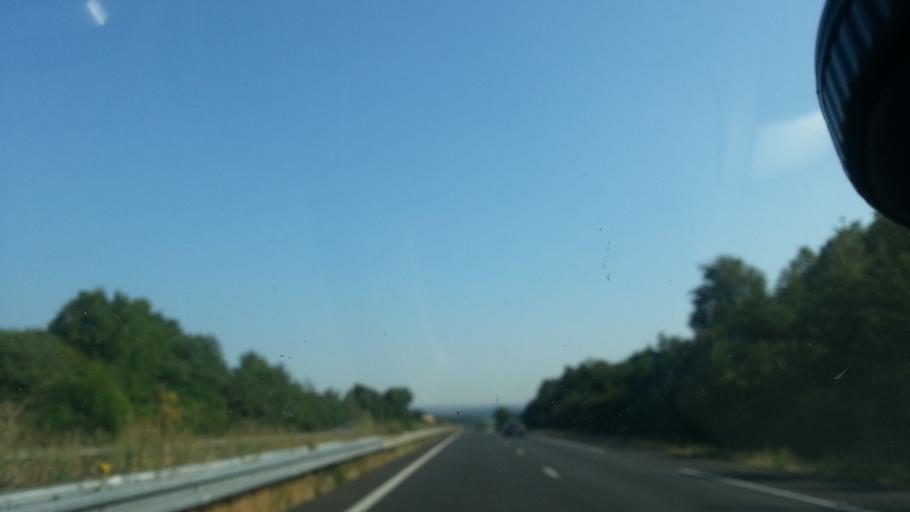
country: FR
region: Poitou-Charentes
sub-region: Departement de la Vienne
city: Les Ormes
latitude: 46.9857
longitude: 0.5481
